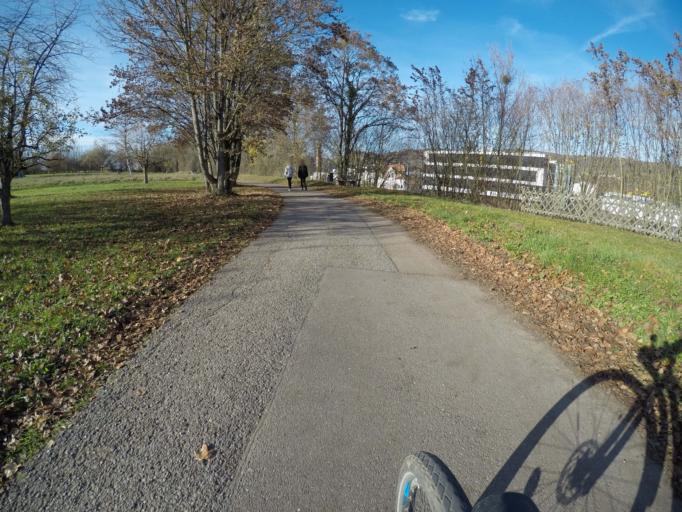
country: DE
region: Baden-Wuerttemberg
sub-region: Regierungsbezirk Stuttgart
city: Winterbach
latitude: 48.8091
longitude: 9.4265
